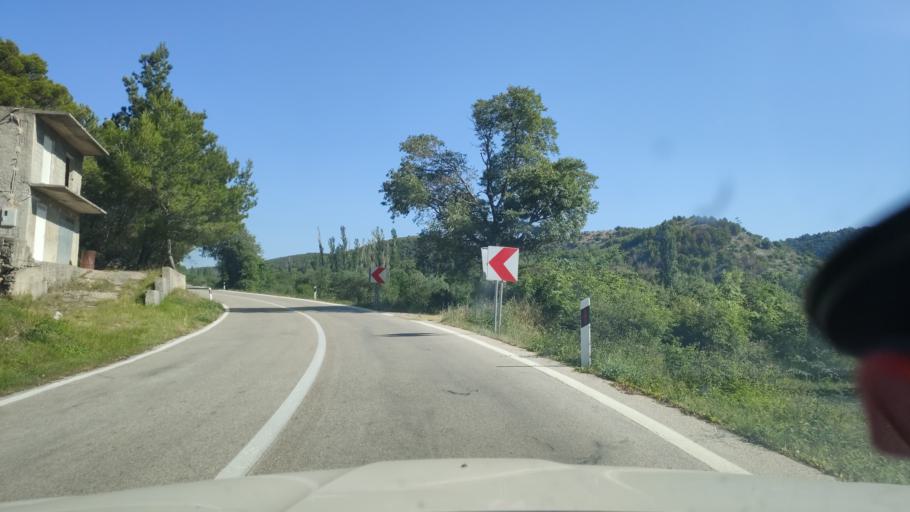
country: HR
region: Sibensko-Kniniska
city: Zaton
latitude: 43.8530
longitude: 15.8975
